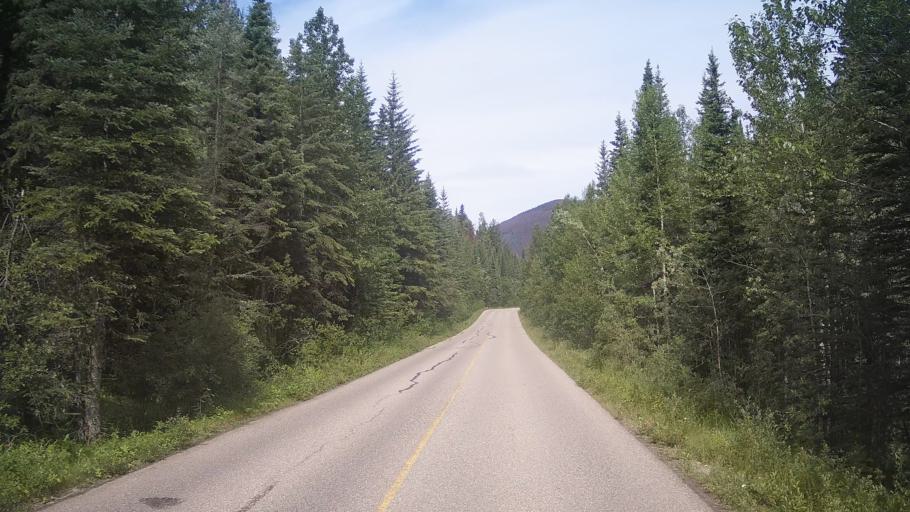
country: CA
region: Alberta
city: Hinton
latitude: 53.1753
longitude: -117.8299
